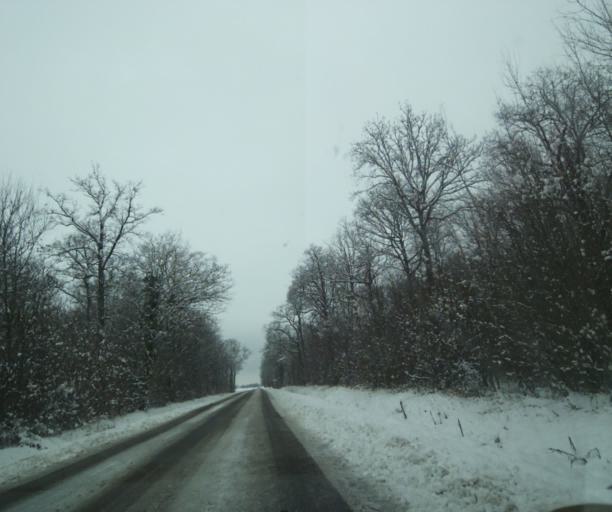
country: FR
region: Champagne-Ardenne
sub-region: Departement de la Haute-Marne
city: Montier-en-Der
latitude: 48.5279
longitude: 4.7489
